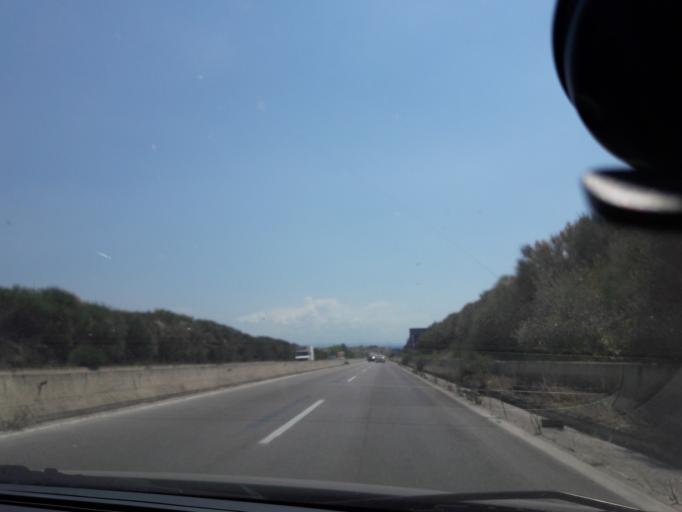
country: GR
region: Central Macedonia
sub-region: Nomos Chalkidikis
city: Nea Triglia
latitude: 40.2934
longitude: 23.1418
